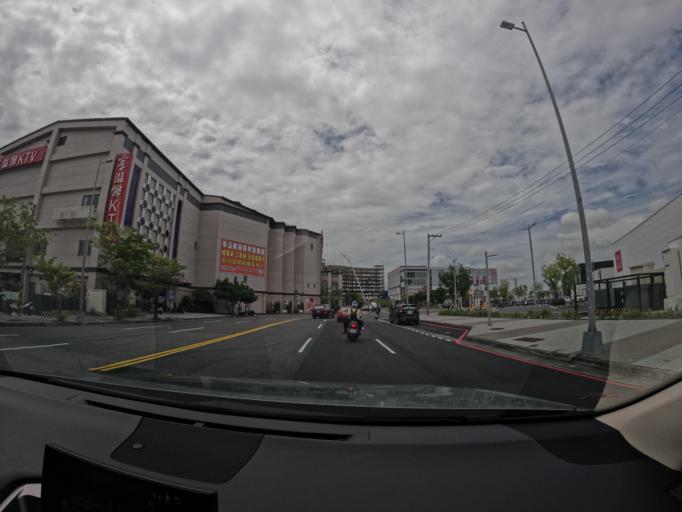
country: TW
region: Kaohsiung
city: Kaohsiung
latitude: 22.7820
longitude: 120.3002
